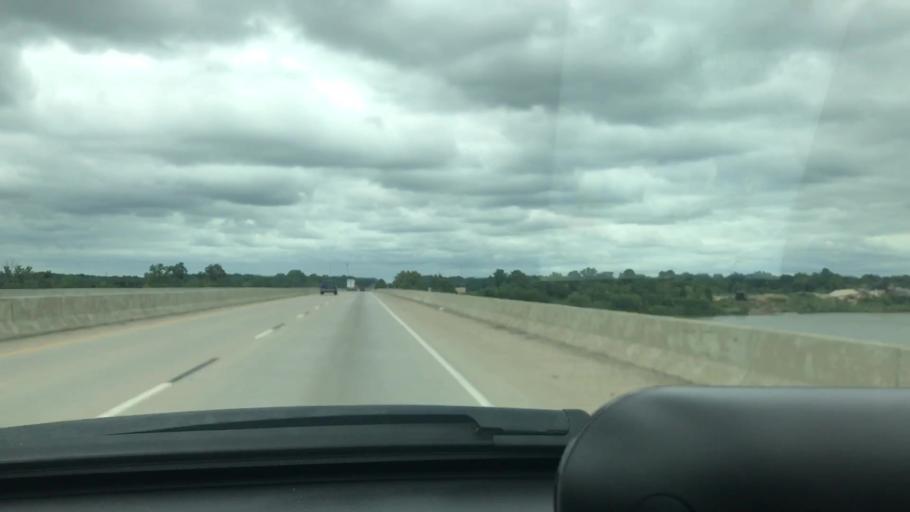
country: US
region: Oklahoma
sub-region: Muskogee County
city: Muskogee
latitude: 35.8059
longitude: -95.4018
